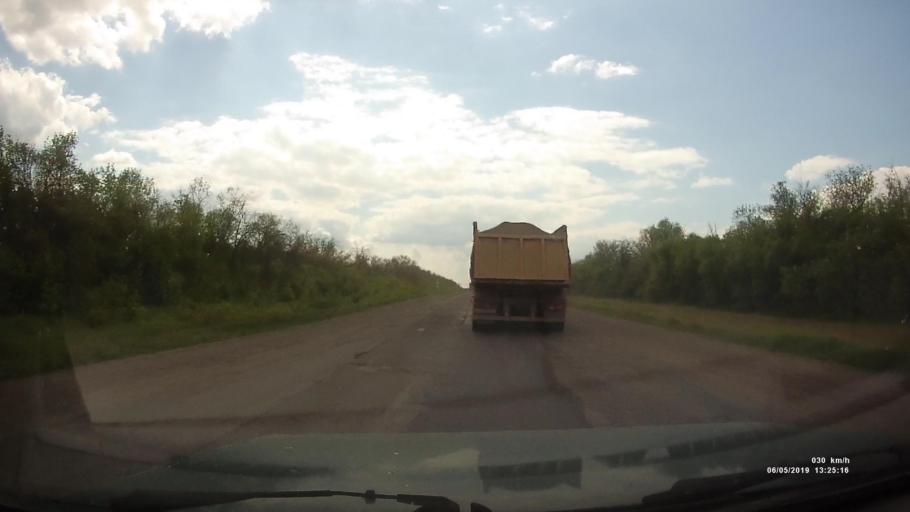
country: RU
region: Rostov
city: Ust'-Donetskiy
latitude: 47.6831
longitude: 40.9053
